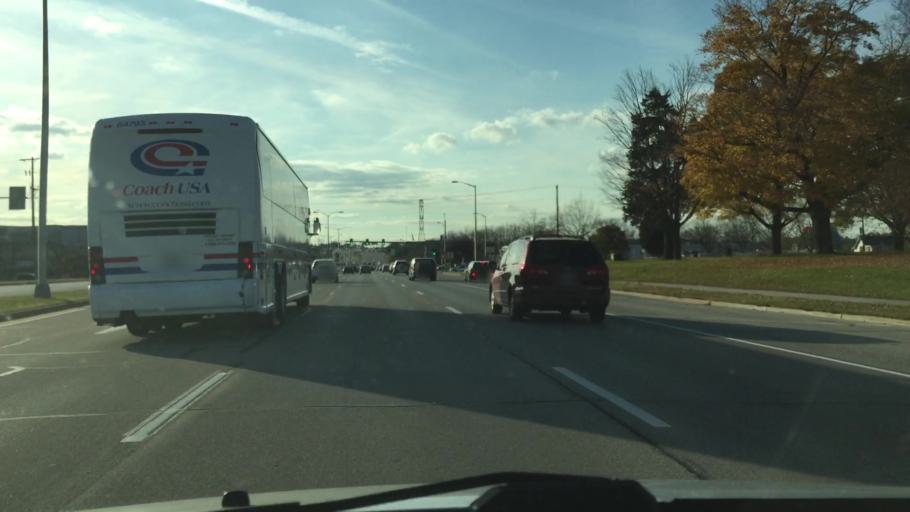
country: US
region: Wisconsin
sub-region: Waukesha County
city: Brookfield
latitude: 43.0362
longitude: -88.1547
